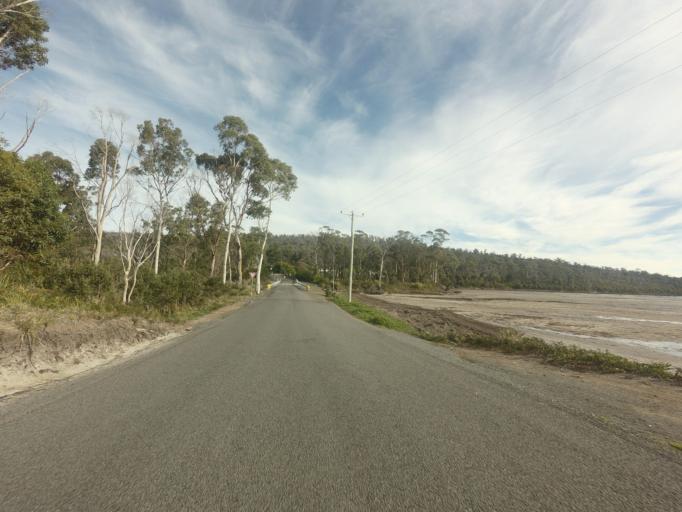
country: AU
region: Tasmania
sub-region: Sorell
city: Sorell
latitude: -42.9574
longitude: 147.8536
